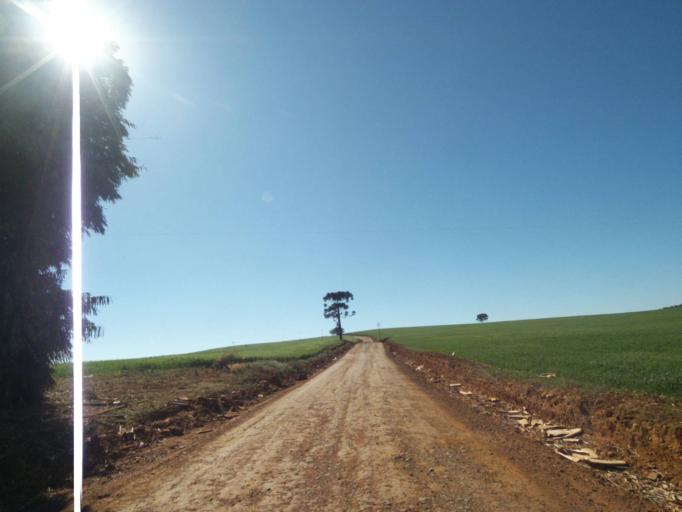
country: BR
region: Parana
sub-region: Tibagi
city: Tibagi
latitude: -24.6079
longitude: -50.6055
